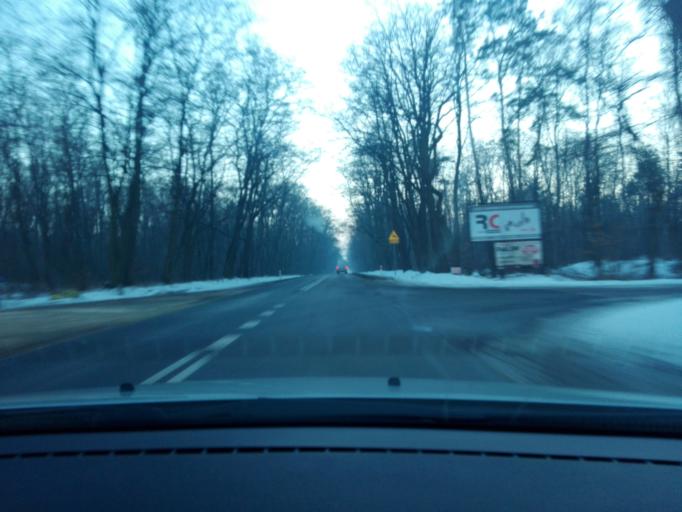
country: PL
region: Lodz Voivodeship
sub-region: Powiat zgierski
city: Zgierz
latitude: 51.9080
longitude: 19.4308
